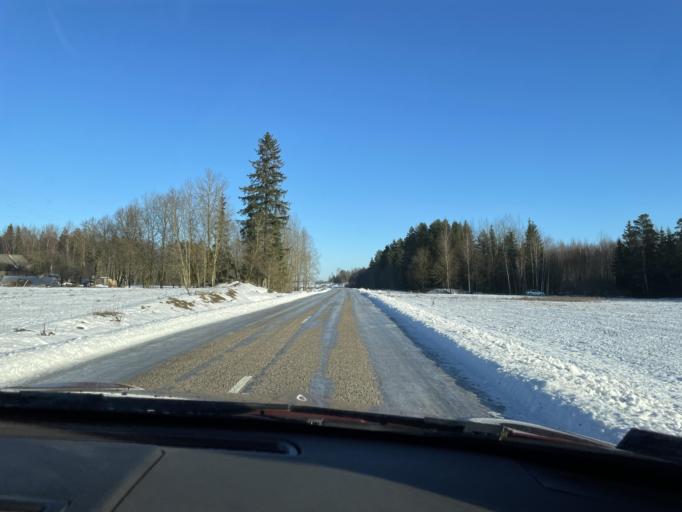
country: LV
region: Ludzas Rajons
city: Ludza
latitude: 56.4477
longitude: 27.5465
